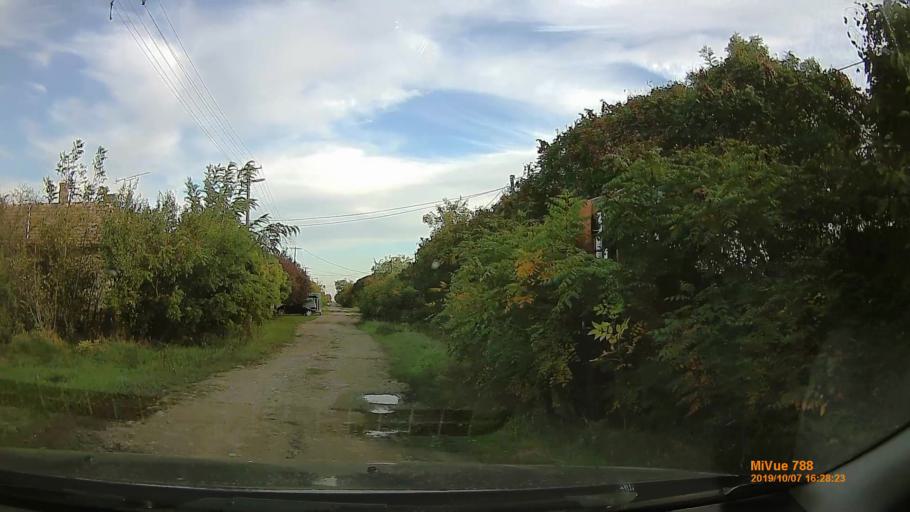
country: HU
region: Bekes
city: Szarvas
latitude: 46.8208
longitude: 20.6470
